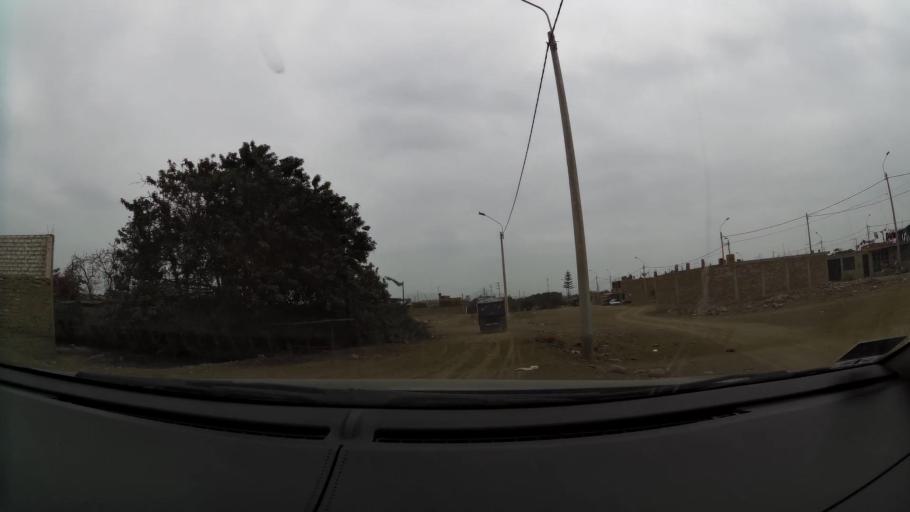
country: PE
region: Lima
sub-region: Provincia de Huaral
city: Huaral
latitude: -11.4861
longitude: -77.2101
